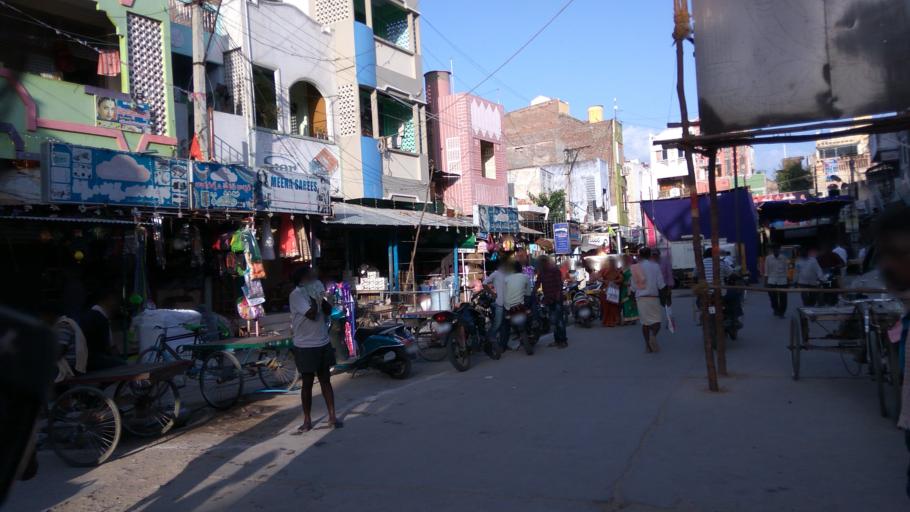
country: IN
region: Andhra Pradesh
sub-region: Prakasam
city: Markapur
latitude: 15.7379
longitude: 79.2720
